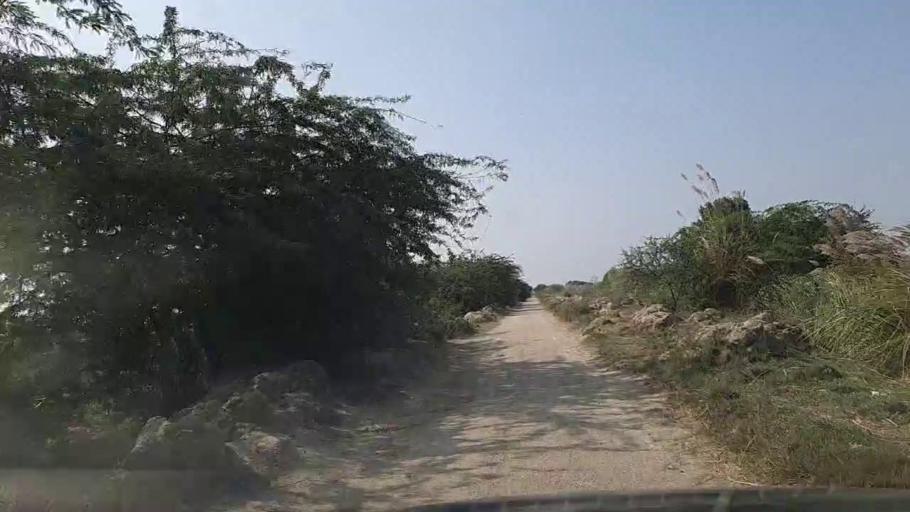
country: PK
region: Sindh
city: Gharo
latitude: 24.6978
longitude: 67.6216
